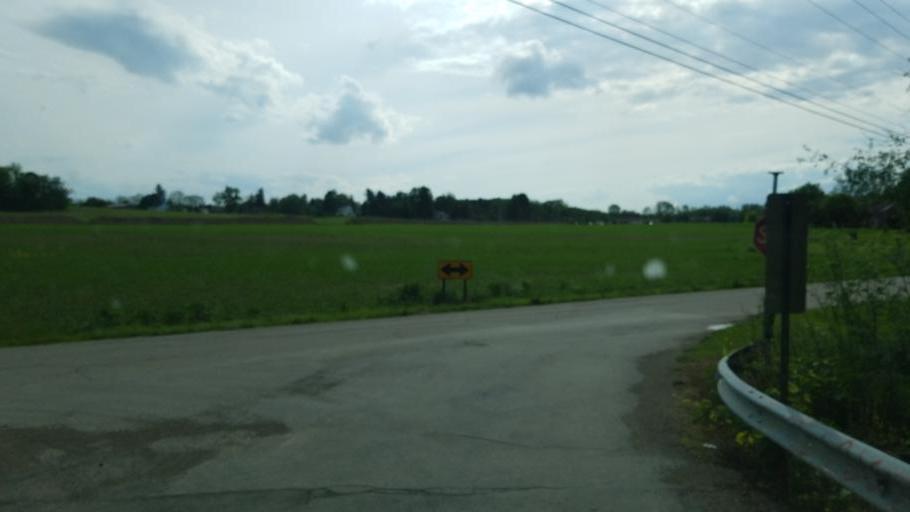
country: US
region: Ohio
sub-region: Richland County
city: Lincoln Heights
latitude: 40.8473
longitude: -82.5083
